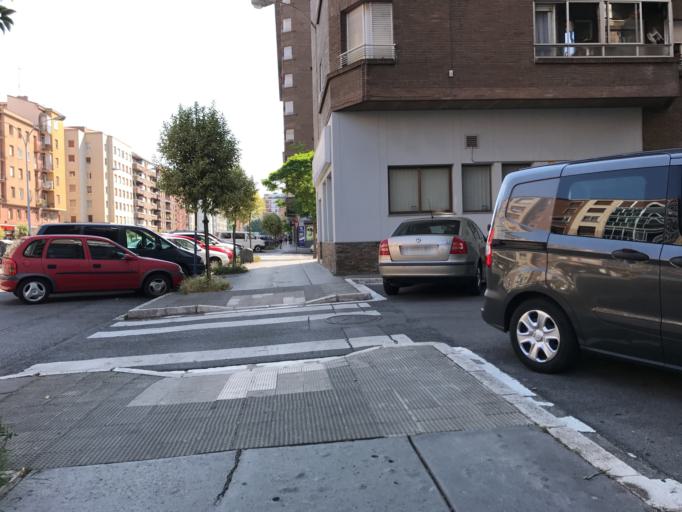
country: ES
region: Basque Country
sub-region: Provincia de Alava
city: Gasteiz / Vitoria
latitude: 42.8568
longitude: -2.6642
